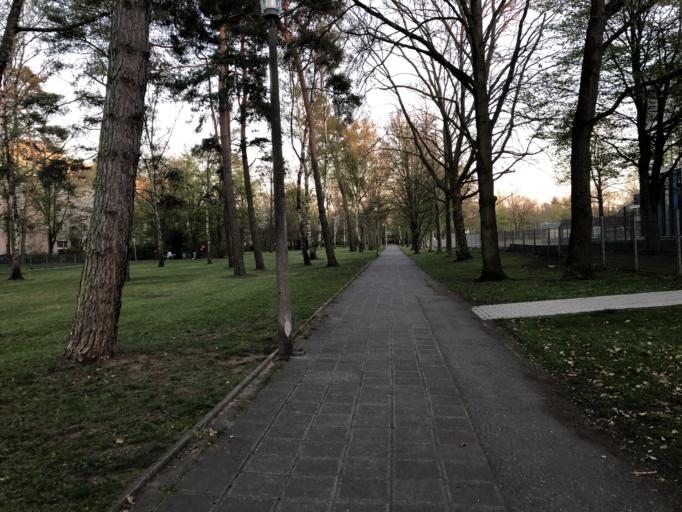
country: DE
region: Bavaria
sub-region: Regierungsbezirk Mittelfranken
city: Nuernberg
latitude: 49.4097
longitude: 11.1180
